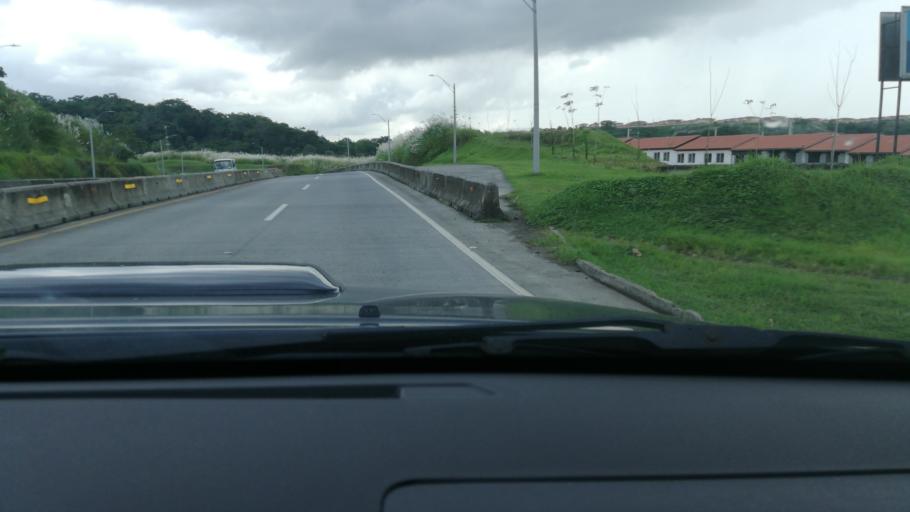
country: PA
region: Panama
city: San Miguelito
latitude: 9.0629
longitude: -79.4747
